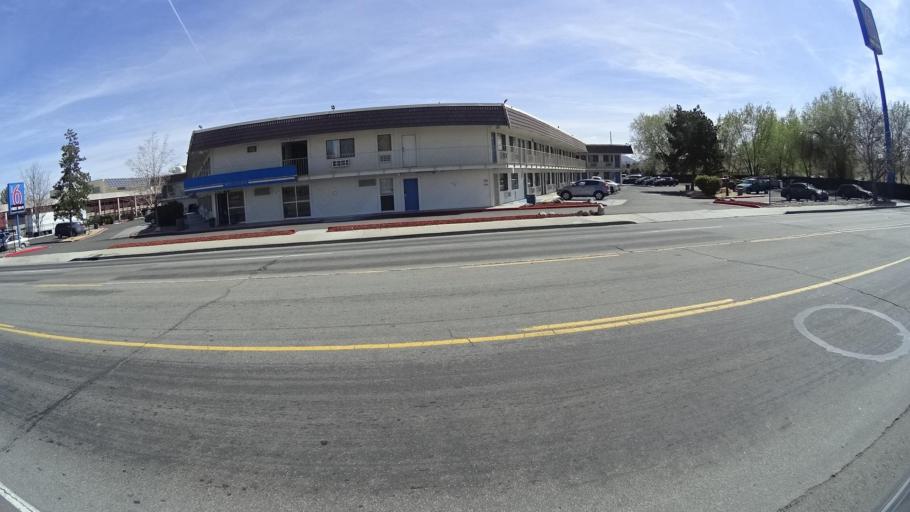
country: US
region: Nevada
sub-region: Washoe County
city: Reno
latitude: 39.5378
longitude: -119.8036
